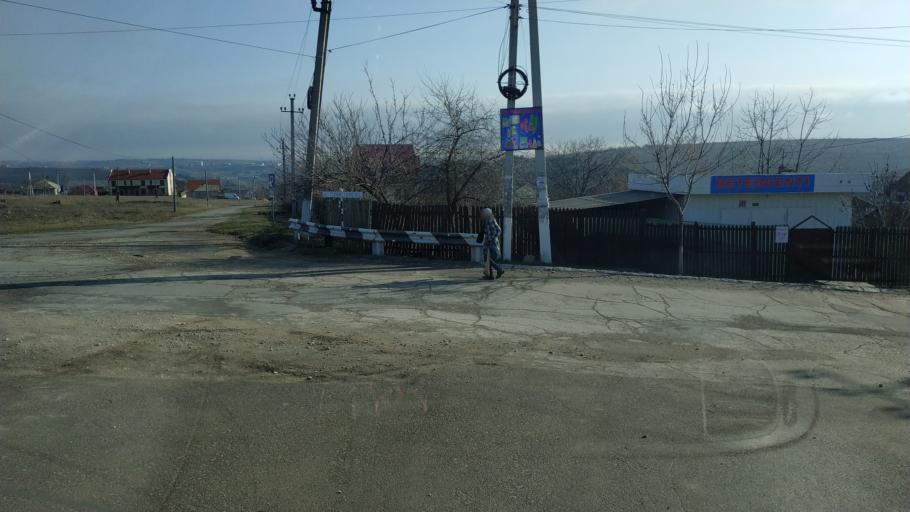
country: MD
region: Laloveni
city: Ialoveni
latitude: 46.9440
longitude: 28.7228
